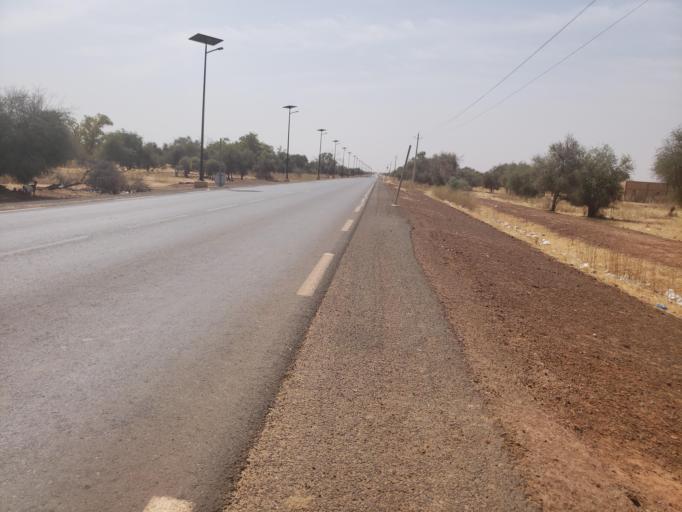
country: SN
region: Matam
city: Ranerou
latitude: 15.2932
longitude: -13.9599
